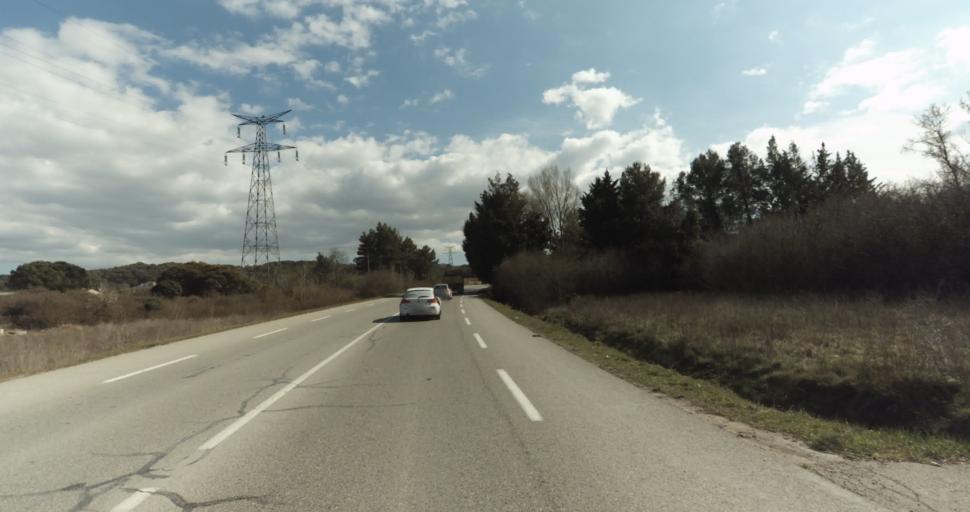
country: FR
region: Provence-Alpes-Cote d'Azur
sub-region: Departement des Bouches-du-Rhone
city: Gardanne
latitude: 43.4627
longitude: 5.4874
